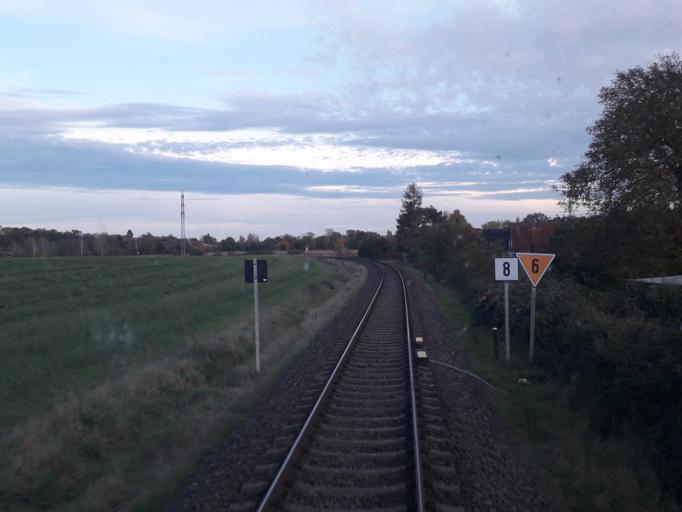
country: DE
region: Brandenburg
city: Neuruppin
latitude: 52.9241
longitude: 12.7837
